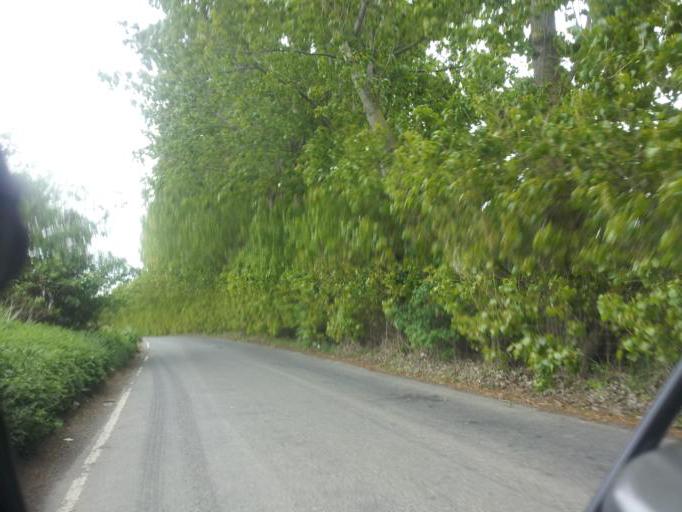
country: GB
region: England
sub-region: Kent
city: Sittingbourne
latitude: 51.3832
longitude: 0.7120
